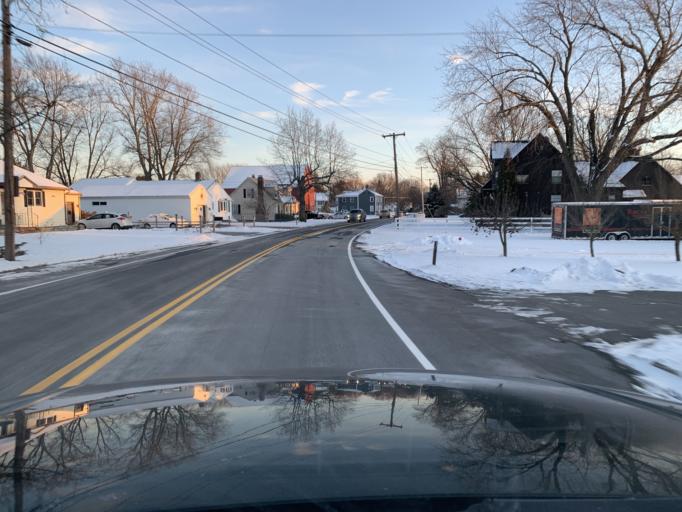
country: US
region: Massachusetts
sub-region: Essex County
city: Haverhill
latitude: 42.7874
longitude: -71.1112
